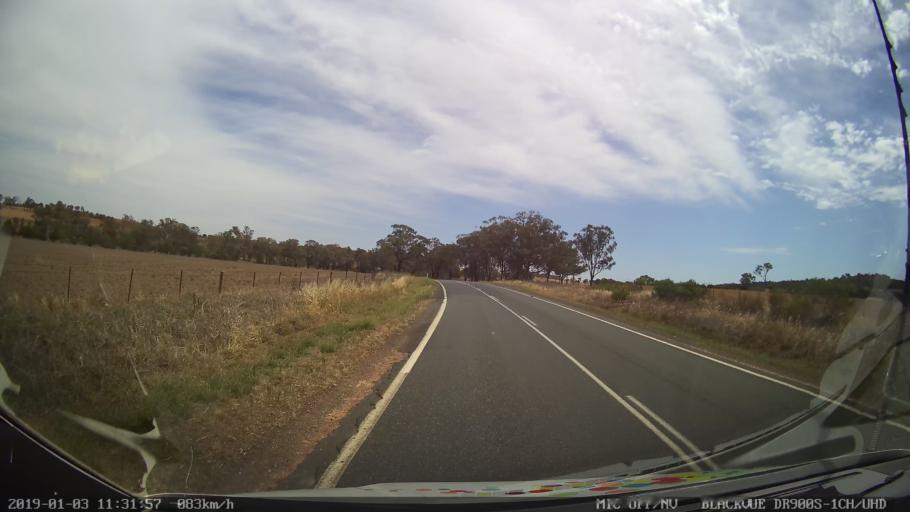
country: AU
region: New South Wales
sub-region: Weddin
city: Grenfell
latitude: -33.9642
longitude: 148.1810
